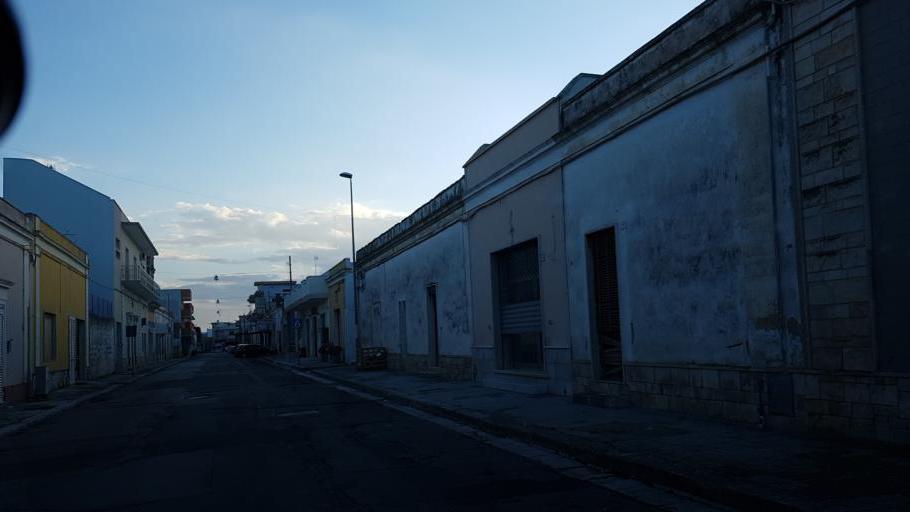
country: IT
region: Apulia
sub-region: Provincia di Lecce
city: Surbo
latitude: 40.3953
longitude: 18.1298
